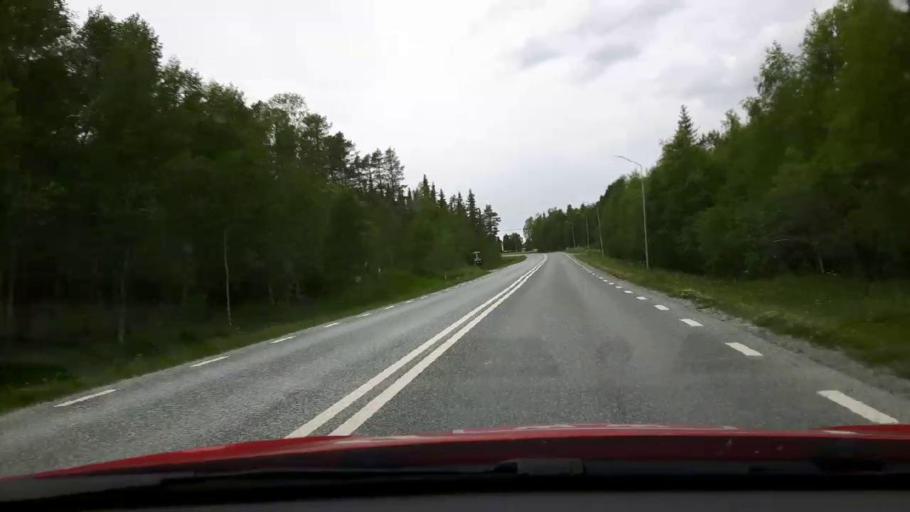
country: NO
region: Hedmark
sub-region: Engerdal
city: Engerdal
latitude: 62.5464
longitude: 12.4797
